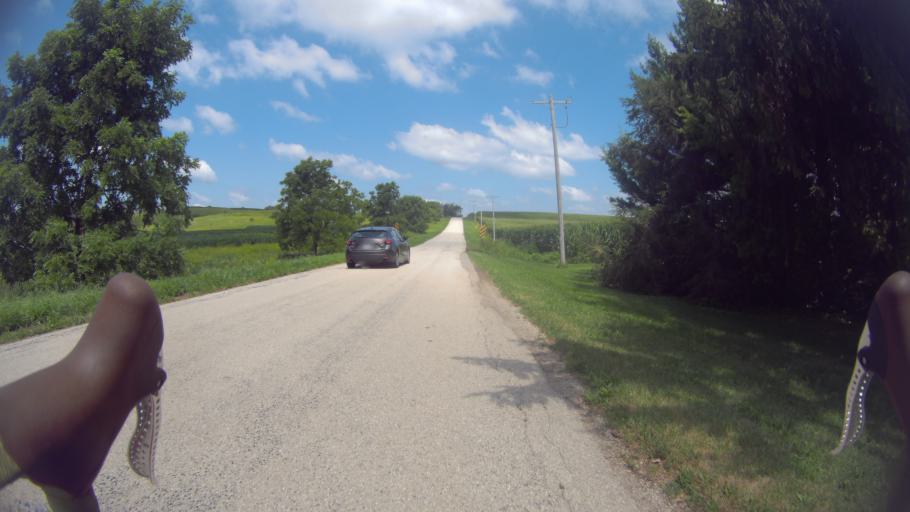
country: US
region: Wisconsin
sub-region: Columbia County
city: Lodi
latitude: 43.2394
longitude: -89.6023
